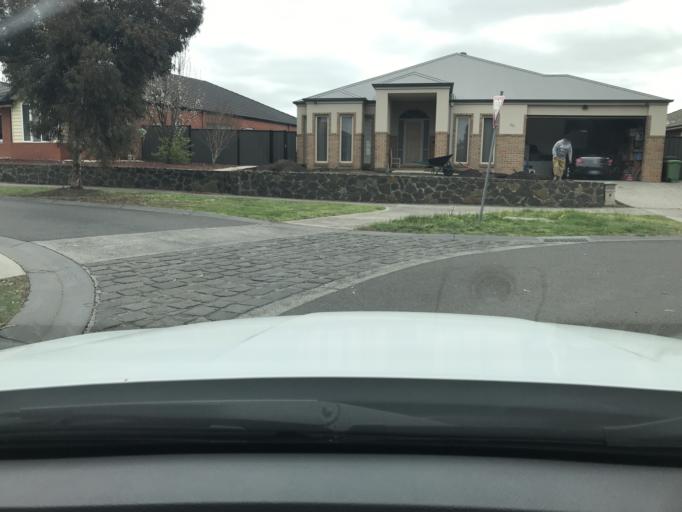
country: AU
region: Victoria
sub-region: Hume
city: Craigieburn
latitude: -37.5804
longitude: 144.9291
